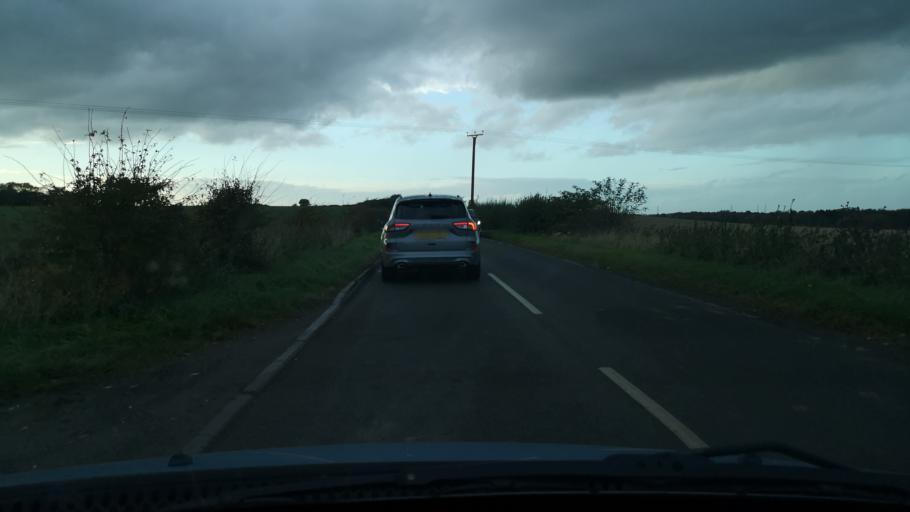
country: GB
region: England
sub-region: Doncaster
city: Norton
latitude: 53.6313
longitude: -1.1907
